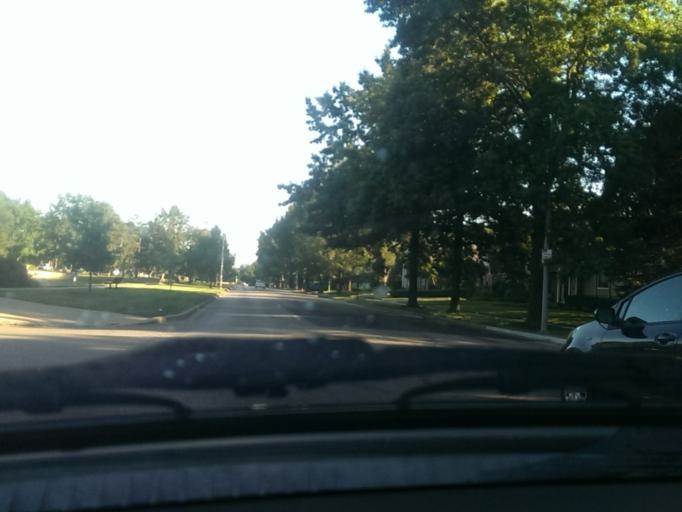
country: US
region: Kansas
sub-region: Johnson County
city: Mission Hills
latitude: 39.0168
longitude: -94.6024
